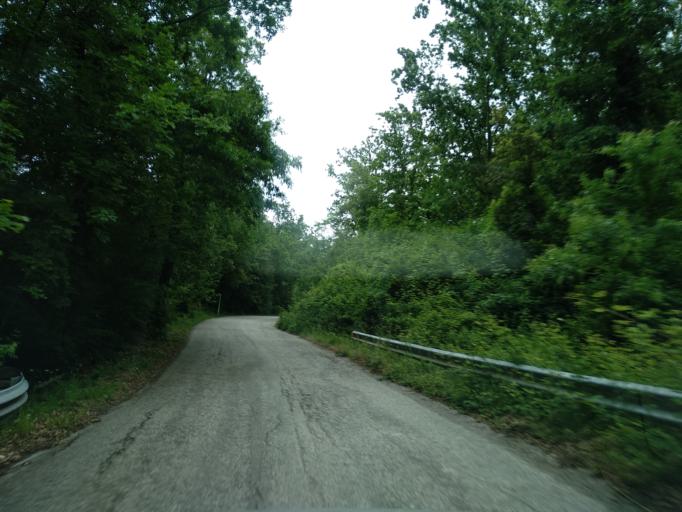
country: IT
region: Tuscany
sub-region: Provincia di Livorno
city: Guasticce
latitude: 43.5676
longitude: 10.4209
